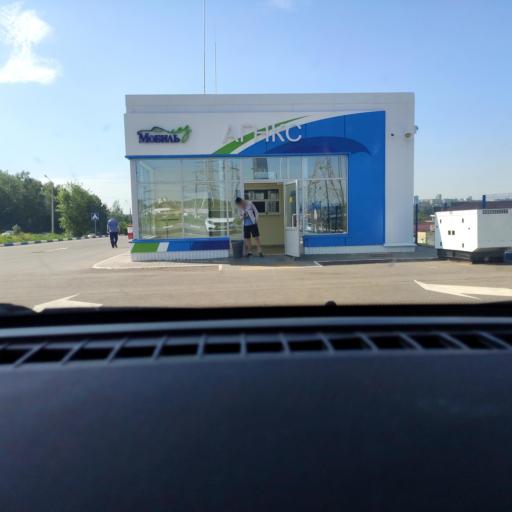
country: RU
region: Udmurtiya
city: Khokhryaki
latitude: 56.8986
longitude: 53.3094
